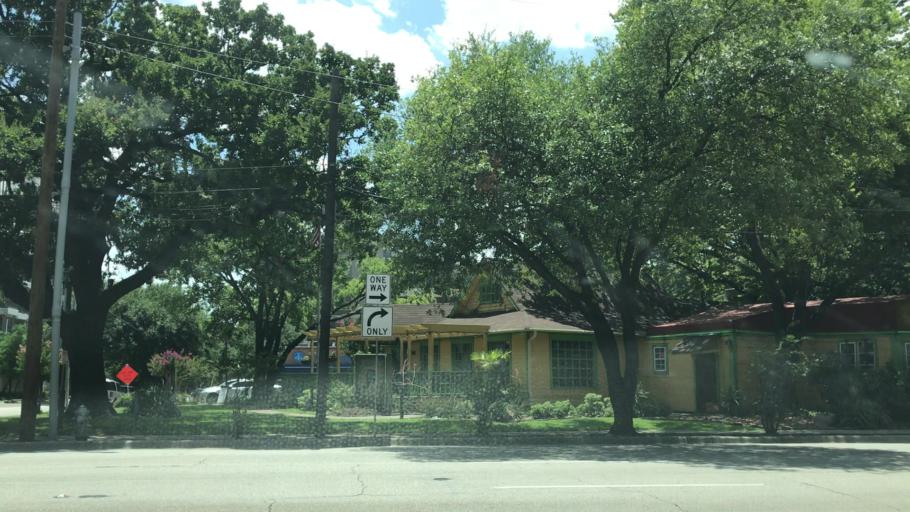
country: US
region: Texas
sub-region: Dallas County
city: Dallas
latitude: 32.8057
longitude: -96.7960
